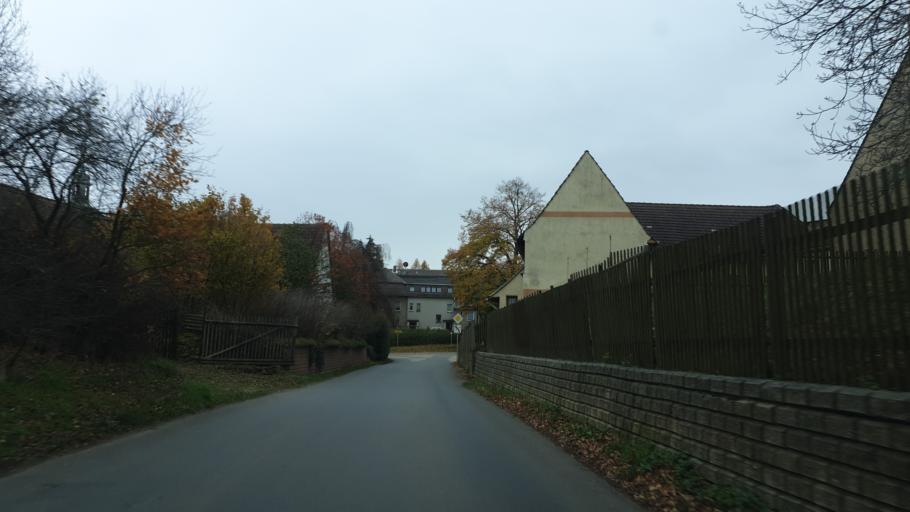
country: DE
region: Thuringia
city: Rauda
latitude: 50.9783
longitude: 11.9402
